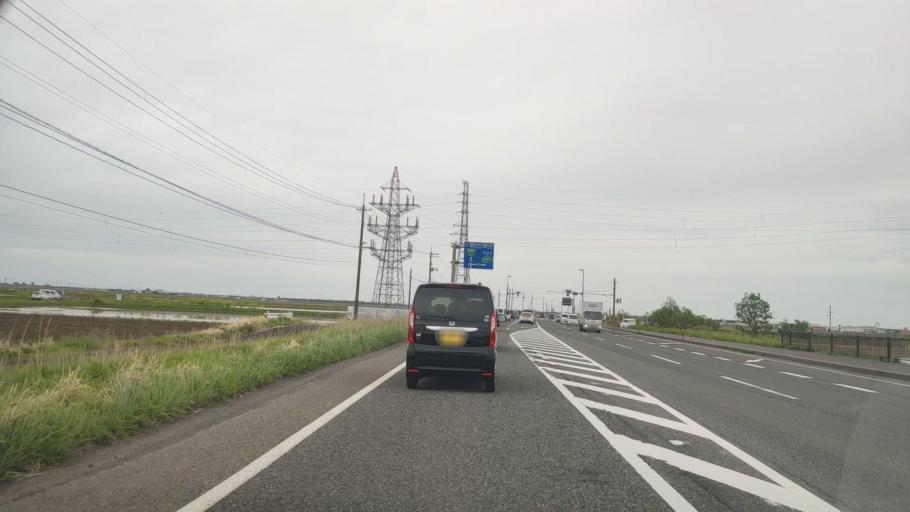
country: JP
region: Niigata
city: Niitsu-honcho
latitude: 37.8018
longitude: 139.1032
